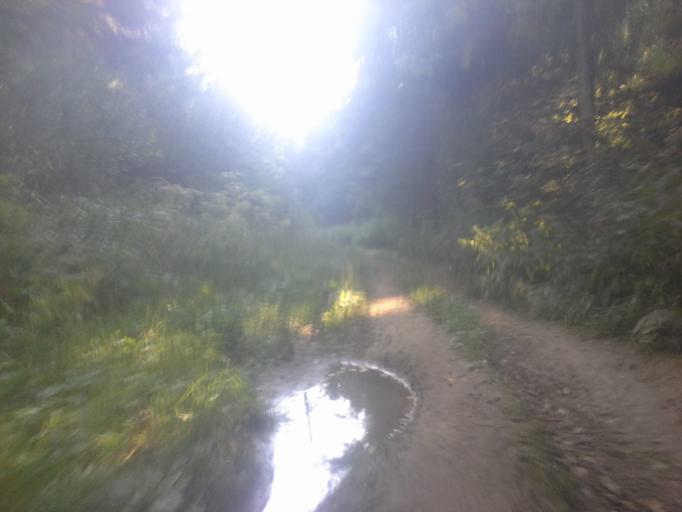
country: RU
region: Moskovskaya
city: Selyatino
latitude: 55.4615
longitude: 36.9874
